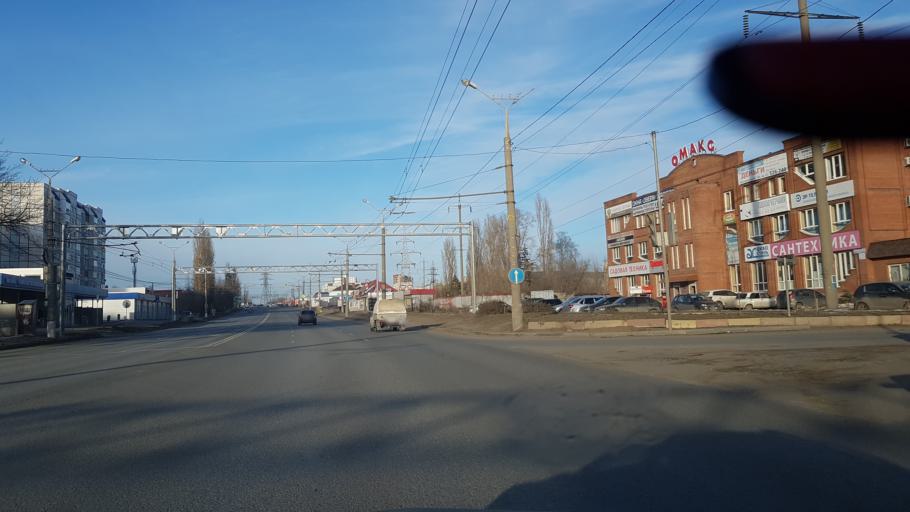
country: RU
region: Samara
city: Tol'yatti
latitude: 53.5313
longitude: 49.3966
